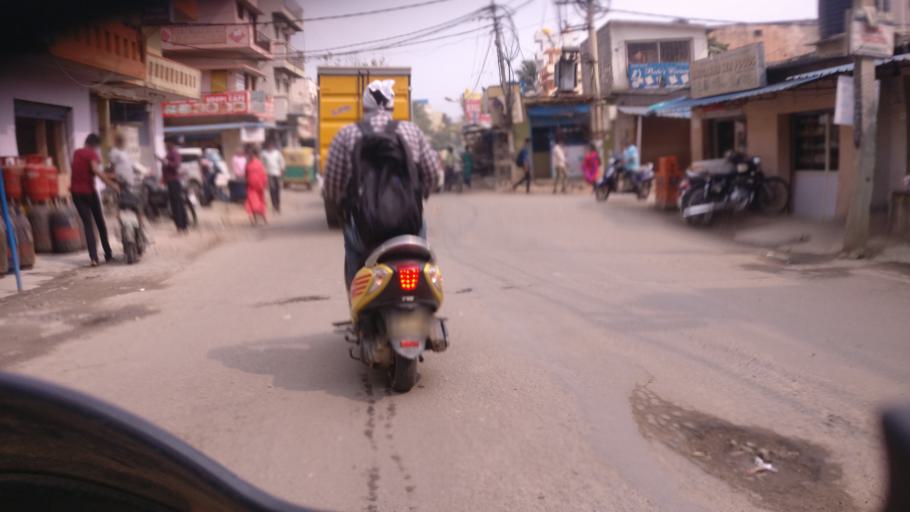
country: IN
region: Karnataka
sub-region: Bangalore Urban
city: Bangalore
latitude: 12.8721
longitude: 77.6541
